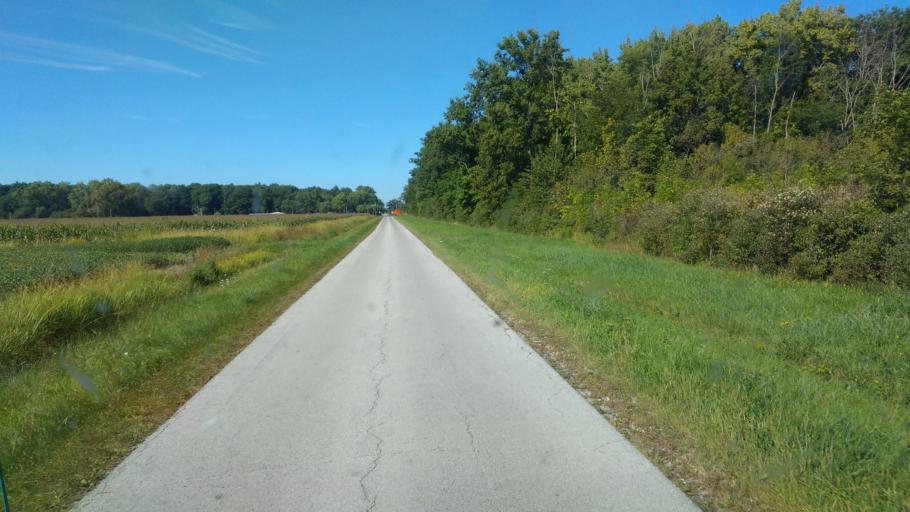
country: US
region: Ohio
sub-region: Sandusky County
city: Clyde
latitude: 41.4048
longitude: -82.9634
